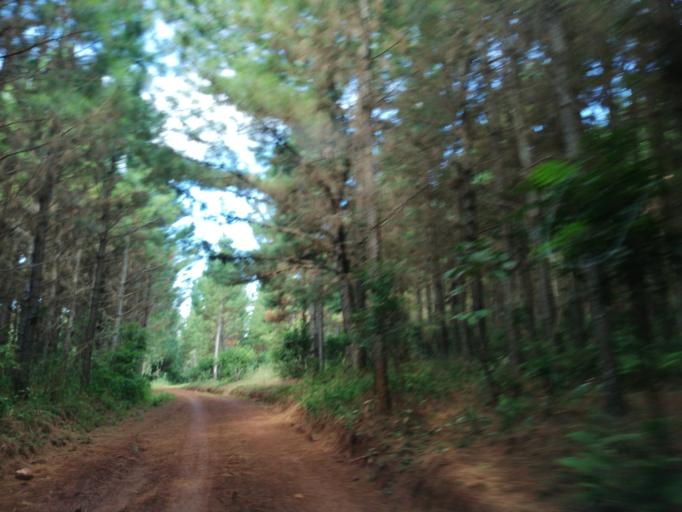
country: AR
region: Misiones
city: Dos de Mayo
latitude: -27.0164
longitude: -54.4182
